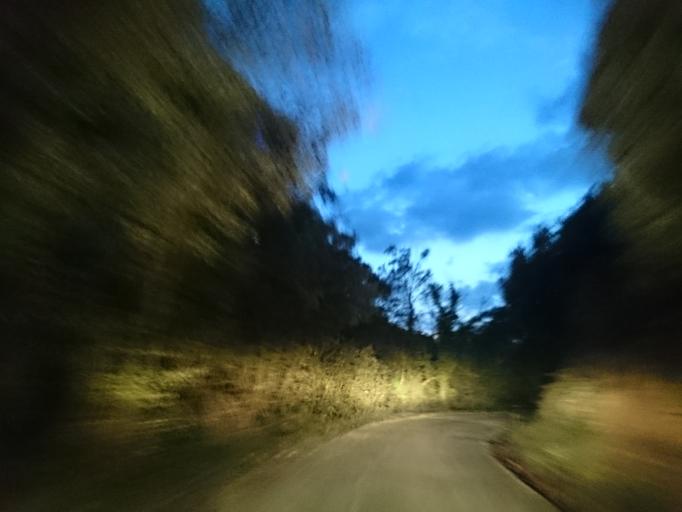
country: ES
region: Catalonia
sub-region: Provincia de Barcelona
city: Tavertet
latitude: 41.9857
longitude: 2.4279
